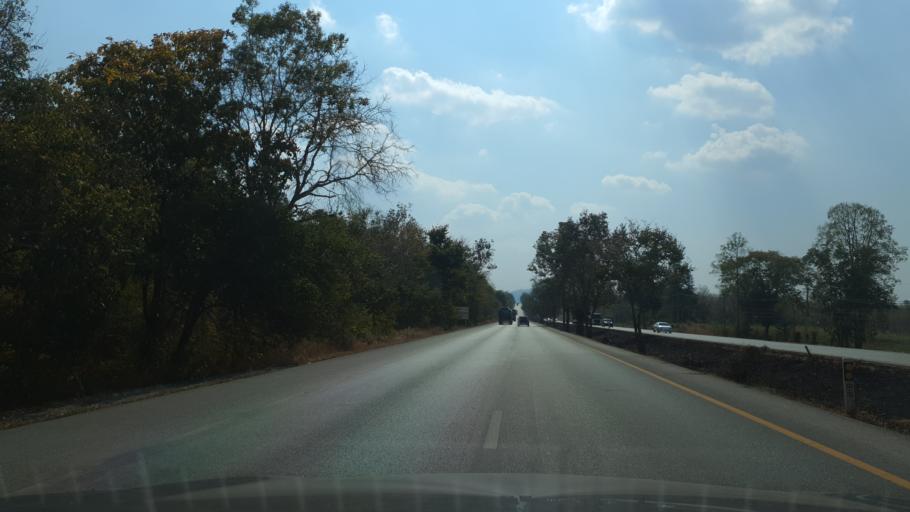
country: TH
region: Lampang
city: Mae Phrik
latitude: 17.3965
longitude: 99.1494
